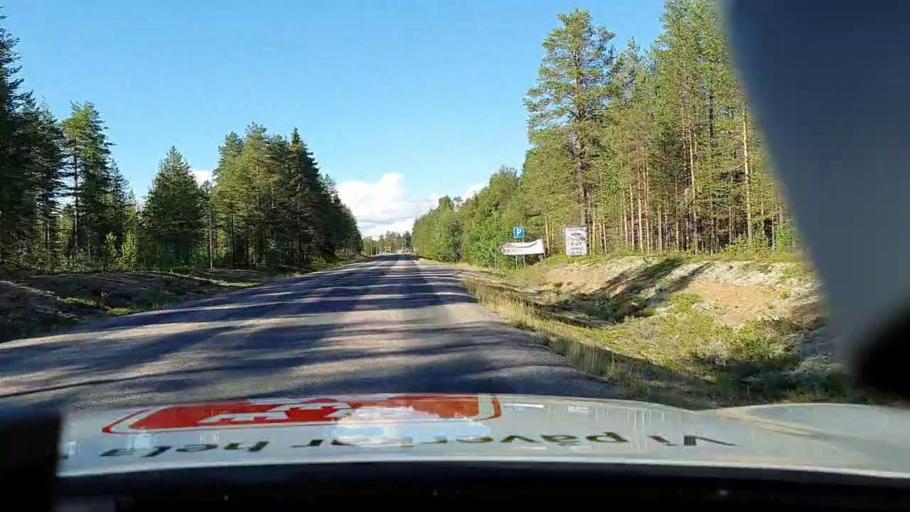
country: SE
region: Norrbotten
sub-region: Overkalix Kommun
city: OEverkalix
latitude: 66.2905
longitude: 22.8171
